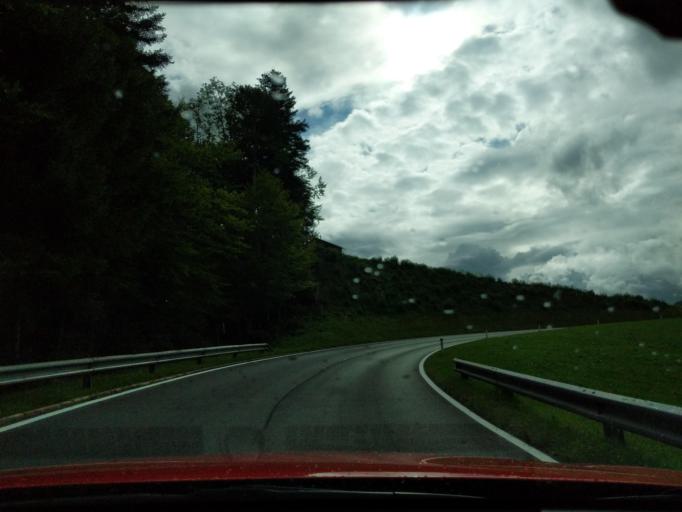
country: AT
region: Vorarlberg
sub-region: Politischer Bezirk Bregenz
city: Riefensberg
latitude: 47.5111
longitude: 9.9555
